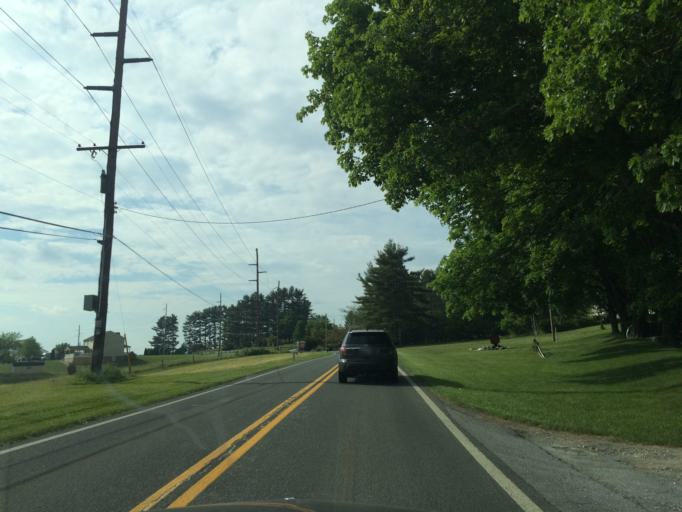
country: US
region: Maryland
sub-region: Baltimore County
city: Reisterstown
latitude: 39.4673
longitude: -76.9008
